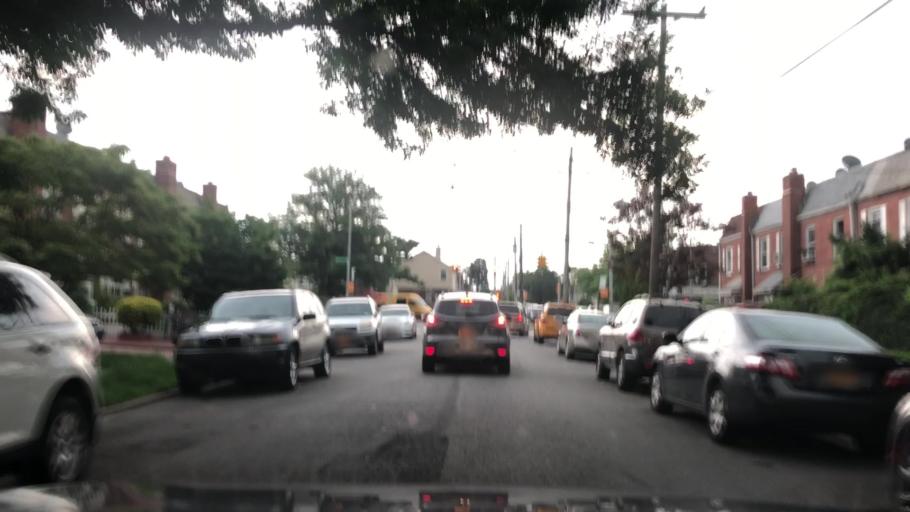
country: US
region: New York
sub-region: Nassau County
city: Bellerose Terrace
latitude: 40.7131
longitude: -73.7327
